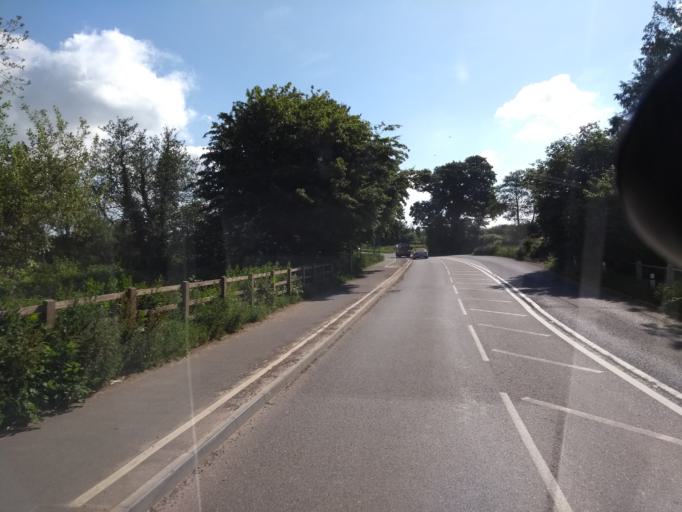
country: GB
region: England
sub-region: Somerset
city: Taunton
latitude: 51.0328
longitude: -3.0773
